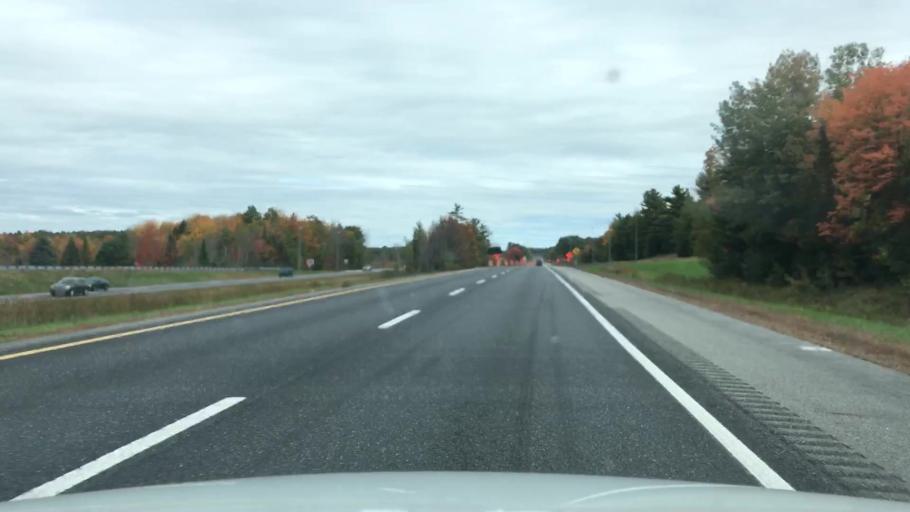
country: US
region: Maine
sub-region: Sagadahoc County
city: Richmond
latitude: 44.1012
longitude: -69.8685
